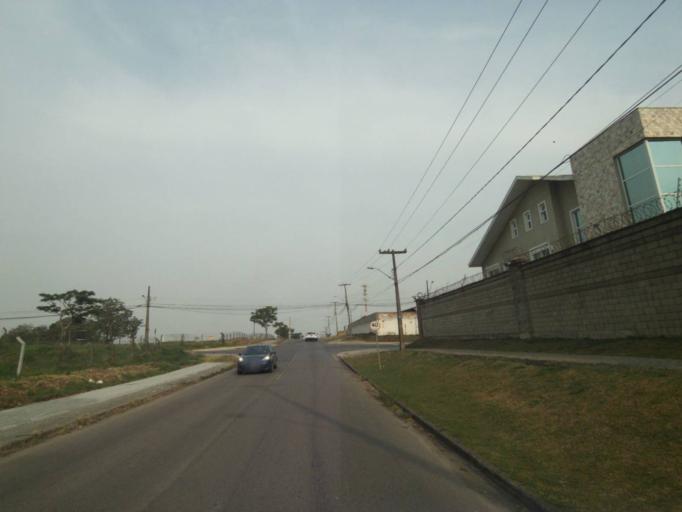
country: BR
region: Parana
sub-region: Sao Jose Dos Pinhais
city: Sao Jose dos Pinhais
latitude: -25.5150
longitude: -49.2822
